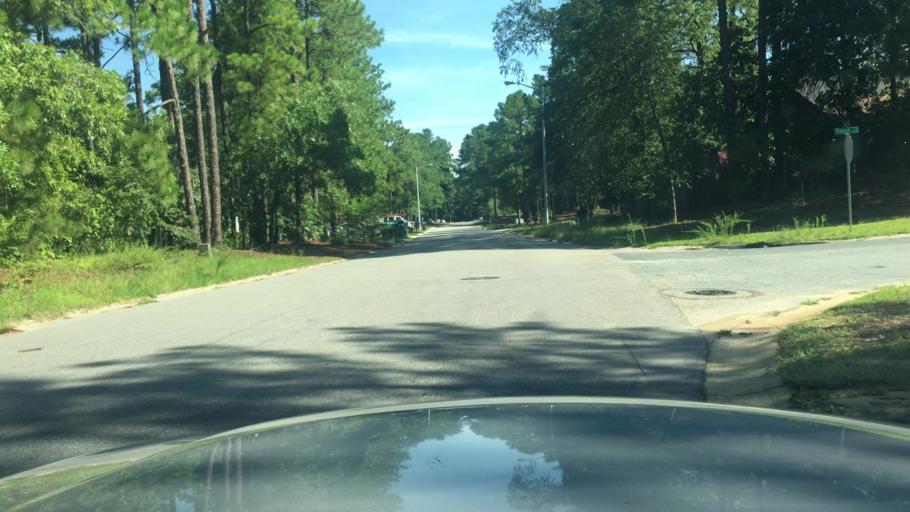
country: US
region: North Carolina
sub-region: Cumberland County
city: Fayetteville
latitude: 35.1105
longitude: -78.9106
